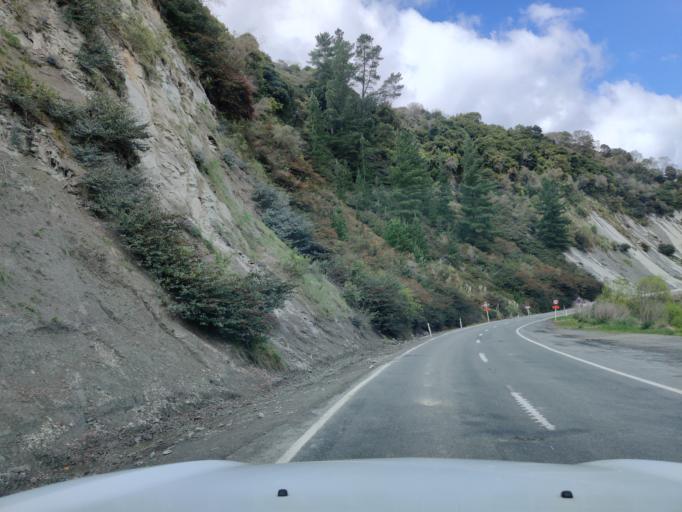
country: NZ
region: Manawatu-Wanganui
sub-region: Ruapehu District
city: Waiouru
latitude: -39.6433
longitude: 175.3264
